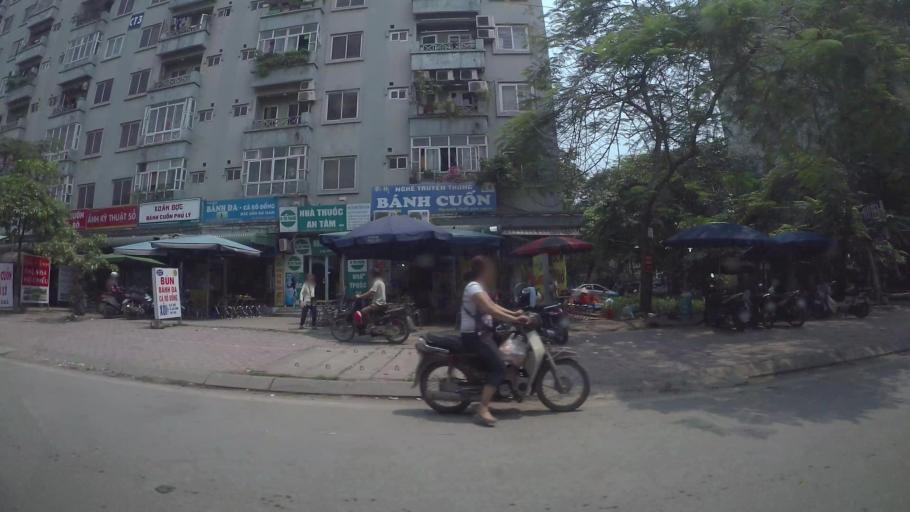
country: VN
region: Ha Noi
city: Van Dien
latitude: 20.9701
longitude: 105.8274
